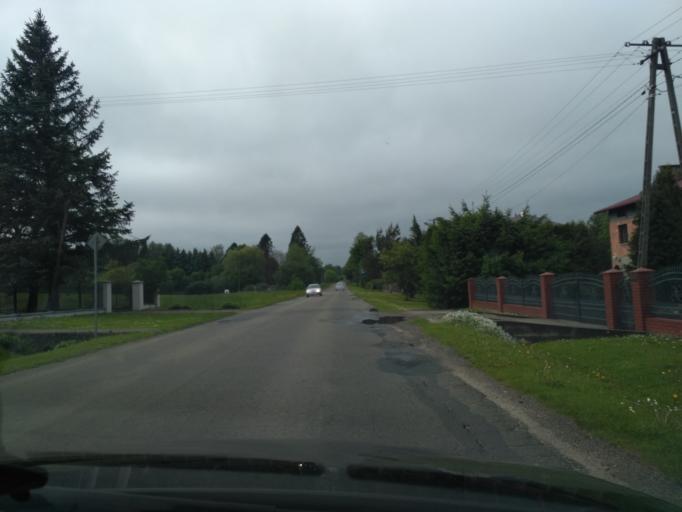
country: PL
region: Subcarpathian Voivodeship
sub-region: Powiat jasielski
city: Brzyska
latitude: 49.8107
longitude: 21.4000
